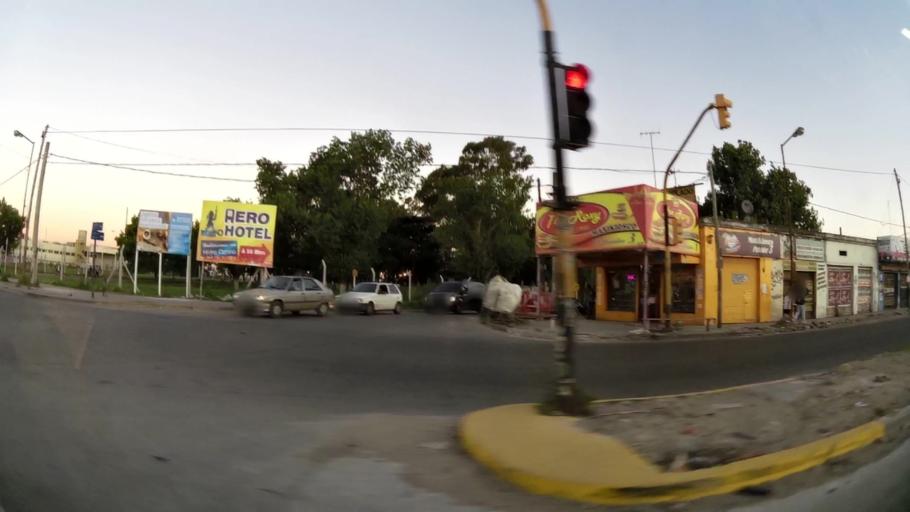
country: AR
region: Buenos Aires
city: San Justo
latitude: -34.7327
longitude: -58.6024
